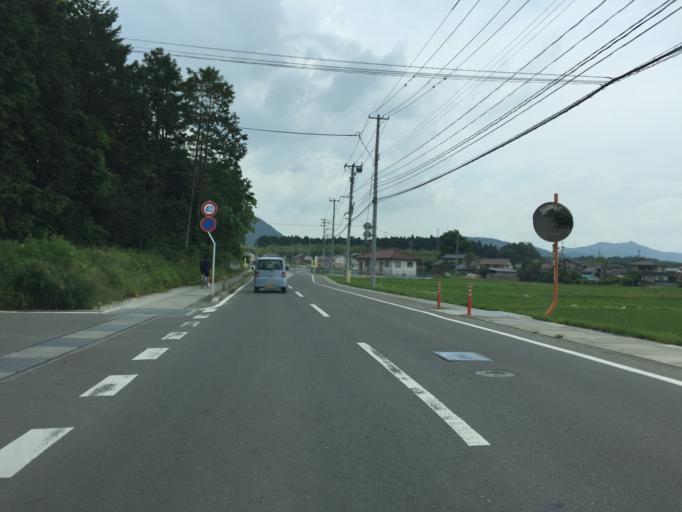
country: JP
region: Miyagi
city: Marumori
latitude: 37.8096
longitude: 140.9012
